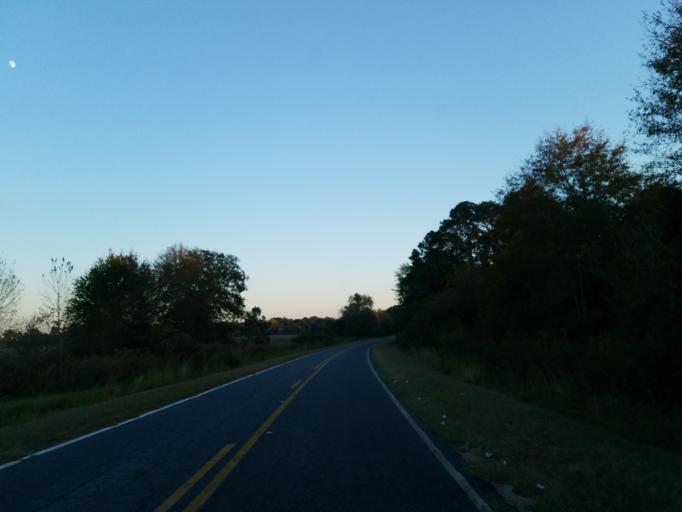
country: US
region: Georgia
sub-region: Ben Hill County
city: Fitzgerald
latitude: 31.6677
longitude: -83.3954
